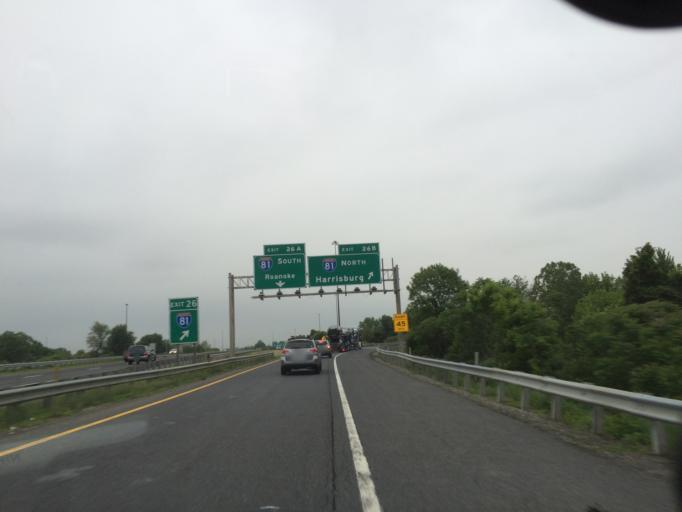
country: US
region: Maryland
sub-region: Washington County
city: Halfway
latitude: 39.6138
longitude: -77.7830
